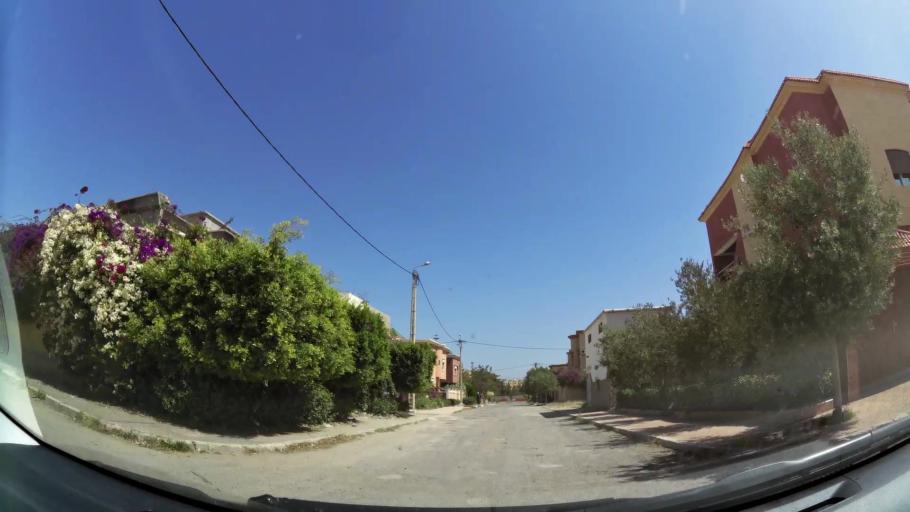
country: MA
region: Souss-Massa-Draa
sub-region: Inezgane-Ait Mellou
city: Inezgane
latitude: 30.3248
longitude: -9.5057
